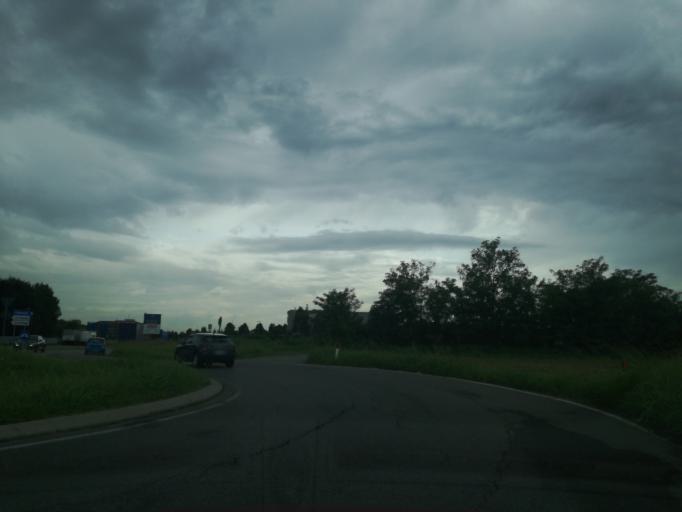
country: IT
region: Lombardy
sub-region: Provincia di Monza e Brianza
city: Ornago
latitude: 45.6077
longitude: 9.4193
